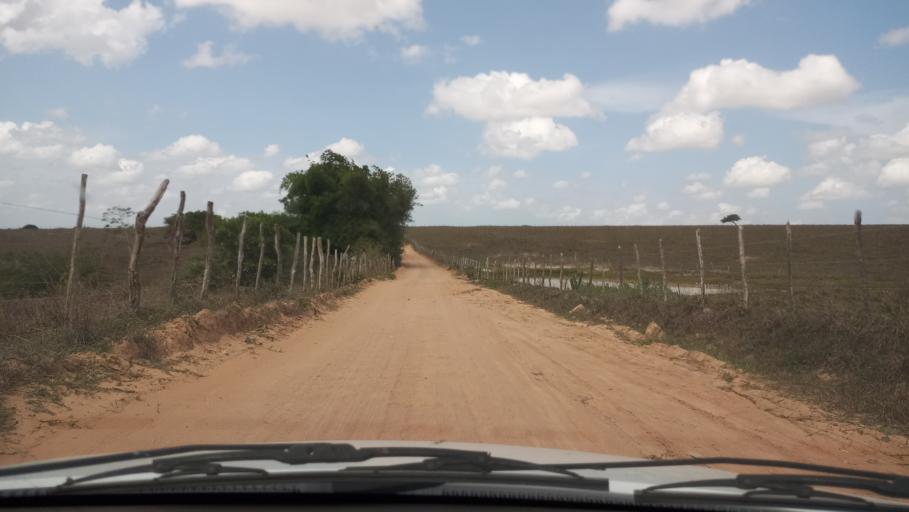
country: BR
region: Rio Grande do Norte
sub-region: Montanhas
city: Montanhas
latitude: -6.3560
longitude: -35.3365
